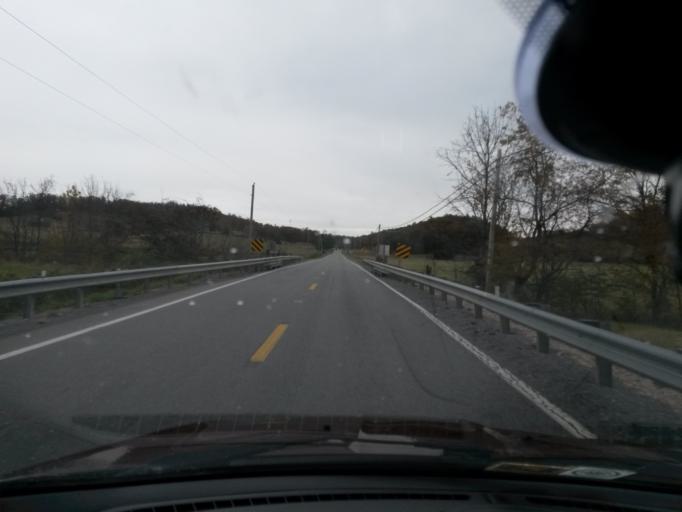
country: US
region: Virginia
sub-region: Alleghany County
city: Clifton Forge
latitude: 37.7451
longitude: -79.7924
